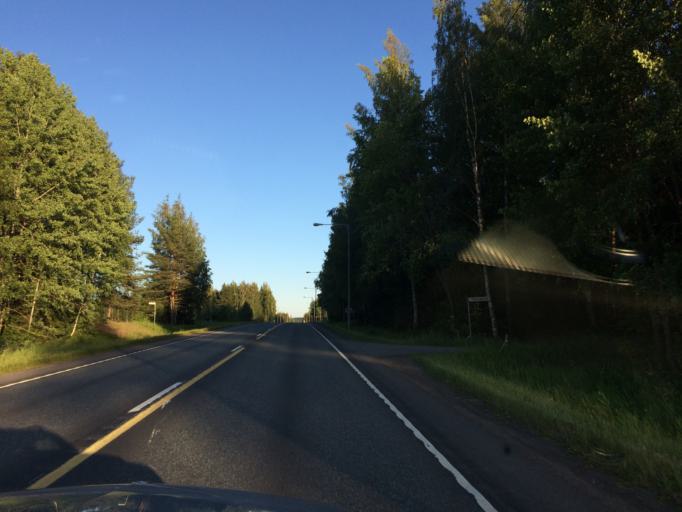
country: FI
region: Haeme
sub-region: Haemeenlinna
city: Tervakoski
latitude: 60.7916
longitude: 24.6741
